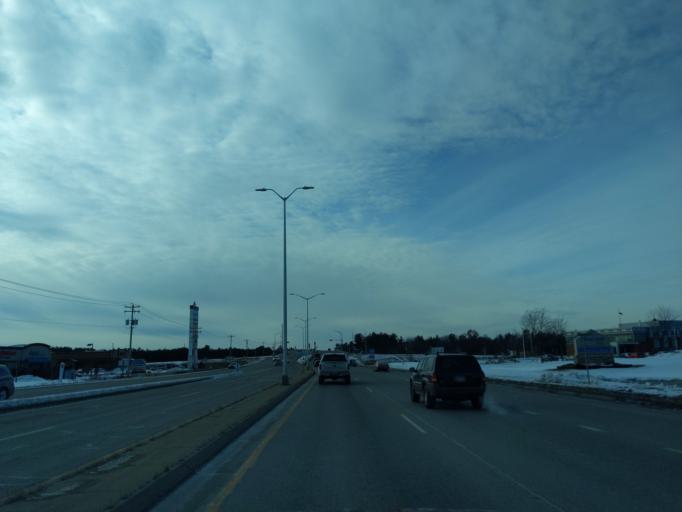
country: US
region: Wisconsin
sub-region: Portage County
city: Whiting
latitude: 44.4973
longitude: -89.5142
